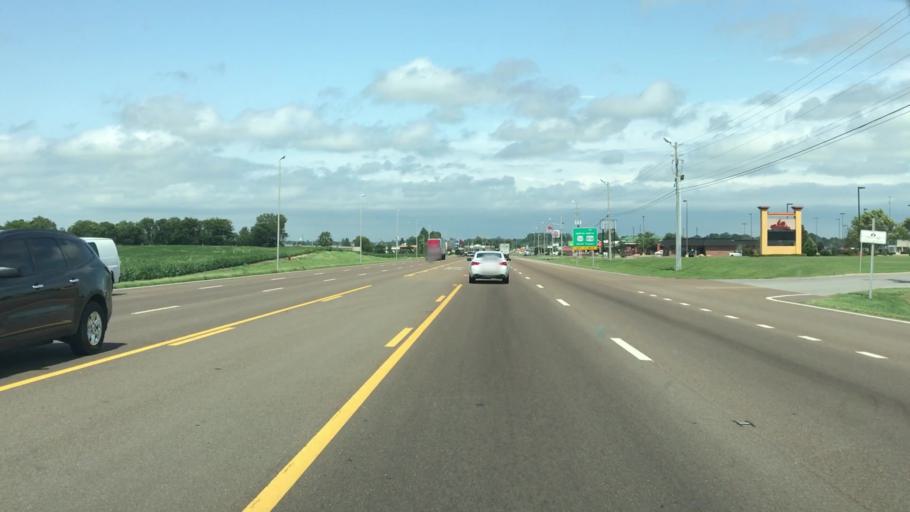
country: US
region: Tennessee
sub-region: Obion County
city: Union City
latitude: 36.4091
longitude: -89.0815
